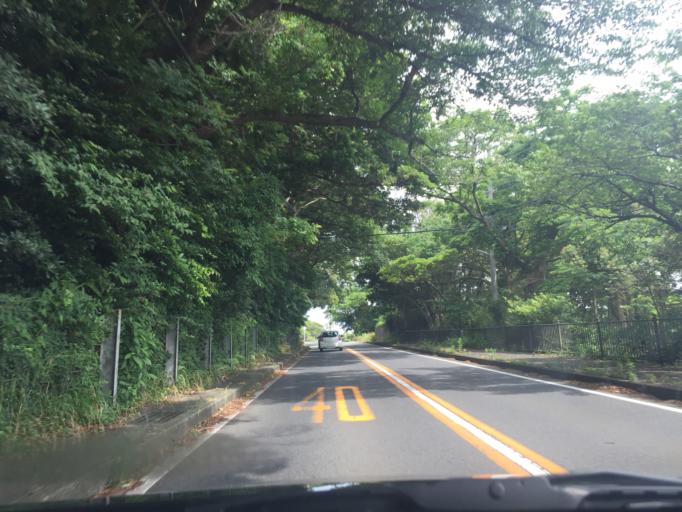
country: JP
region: Shizuoka
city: Shimoda
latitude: 34.7555
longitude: 139.0169
